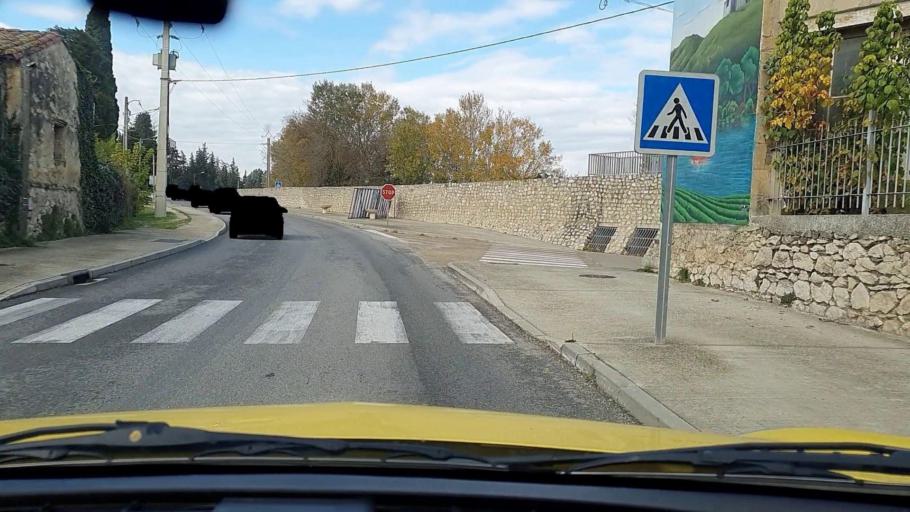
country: FR
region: Languedoc-Roussillon
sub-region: Departement du Gard
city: Comps
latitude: 43.8525
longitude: 4.6011
